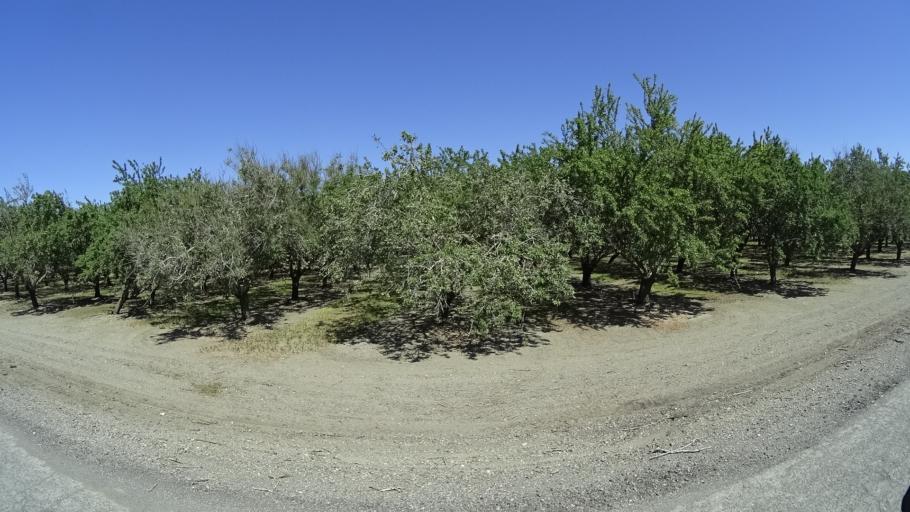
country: US
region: California
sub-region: Glenn County
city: Orland
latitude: 39.7215
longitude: -122.1355
